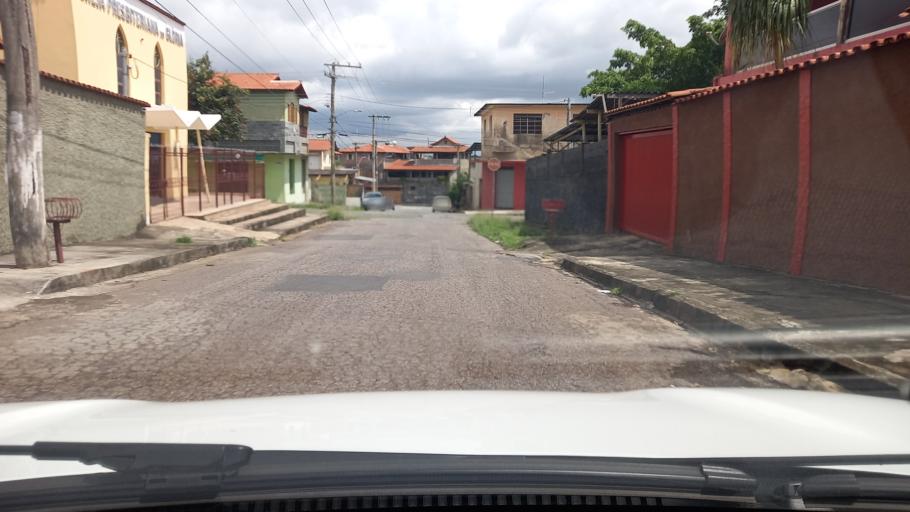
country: BR
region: Minas Gerais
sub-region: Contagem
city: Contagem
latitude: -19.9015
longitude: -44.0132
